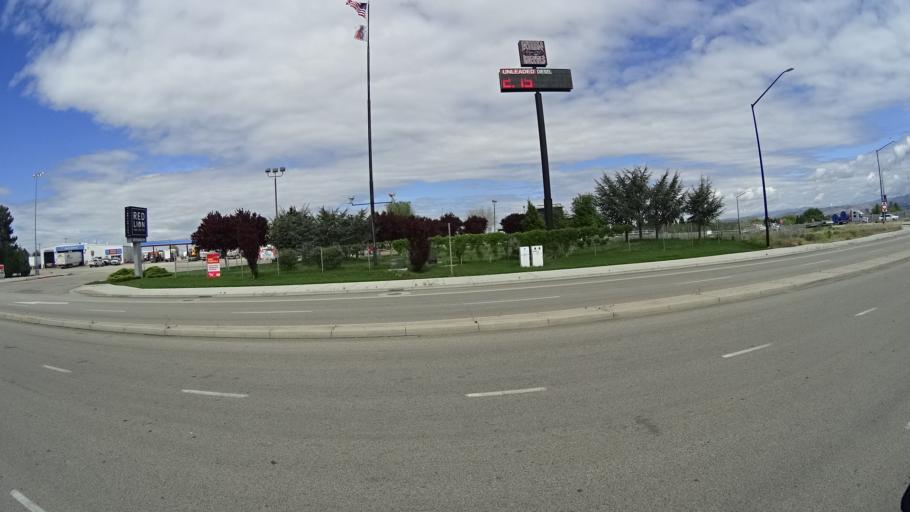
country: US
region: Idaho
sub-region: Ada County
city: Boise
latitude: 43.5650
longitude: -116.1975
